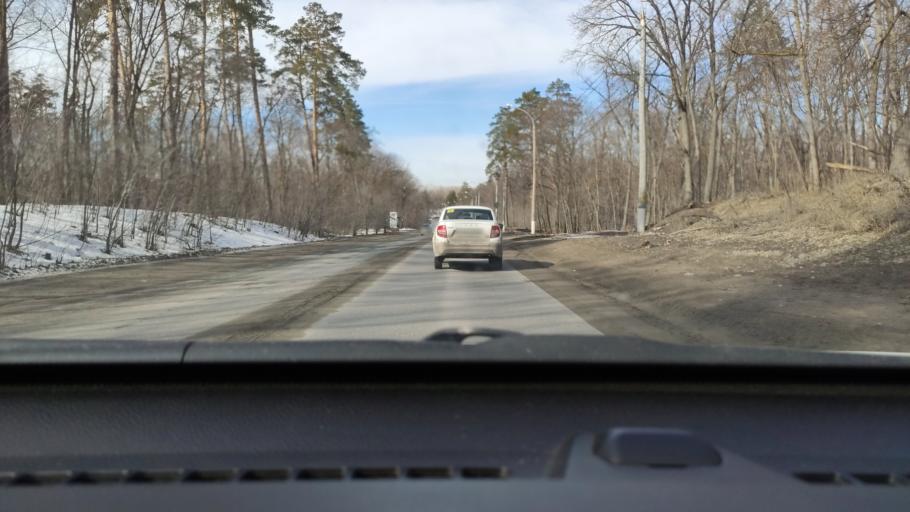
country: RU
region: Samara
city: Tol'yatti
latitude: 53.4942
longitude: 49.2944
